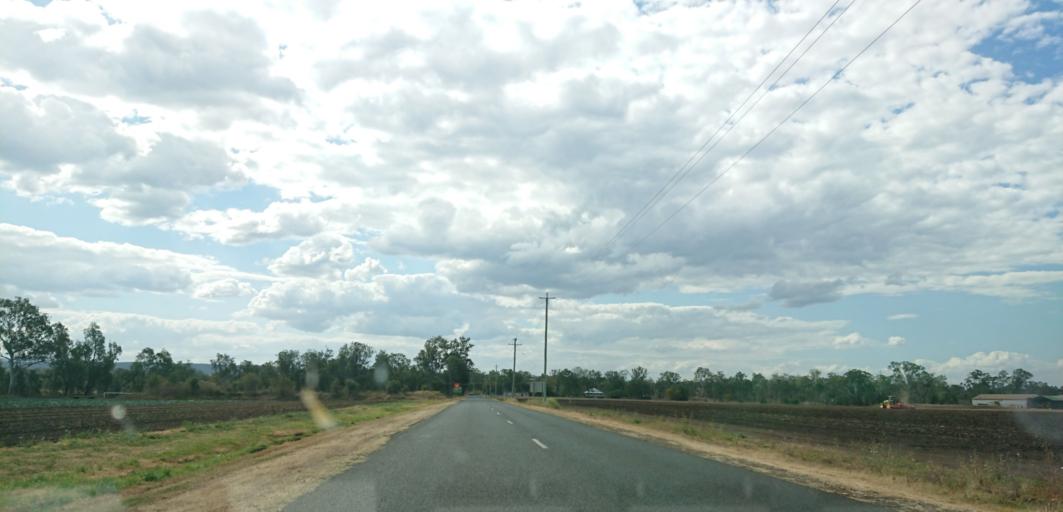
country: AU
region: Queensland
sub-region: Lockyer Valley
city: Gatton
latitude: -27.5773
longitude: 152.2296
